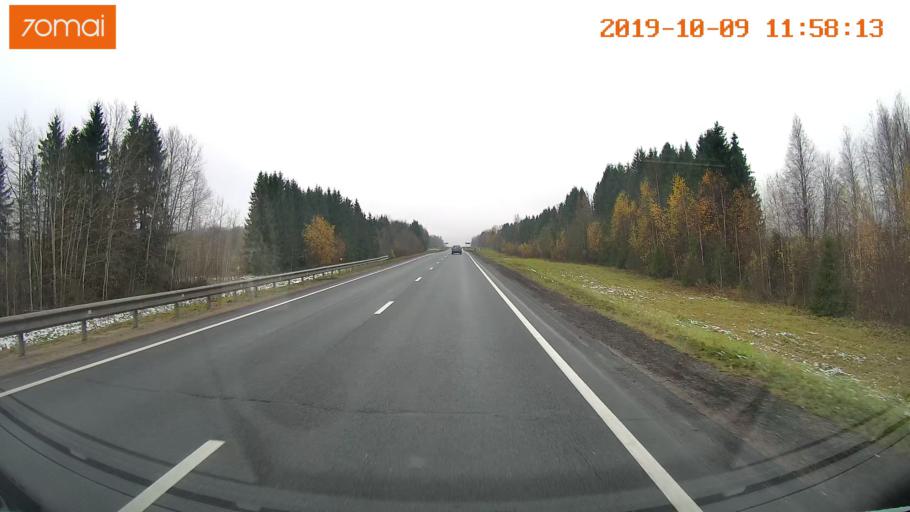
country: RU
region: Vologda
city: Gryazovets
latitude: 58.7212
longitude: 40.2962
